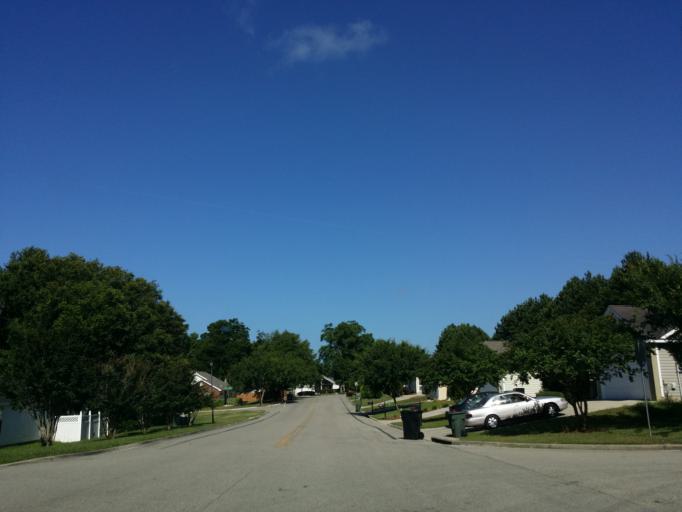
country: US
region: Florida
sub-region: Leon County
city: Tallahassee
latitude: 30.4575
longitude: -84.2192
